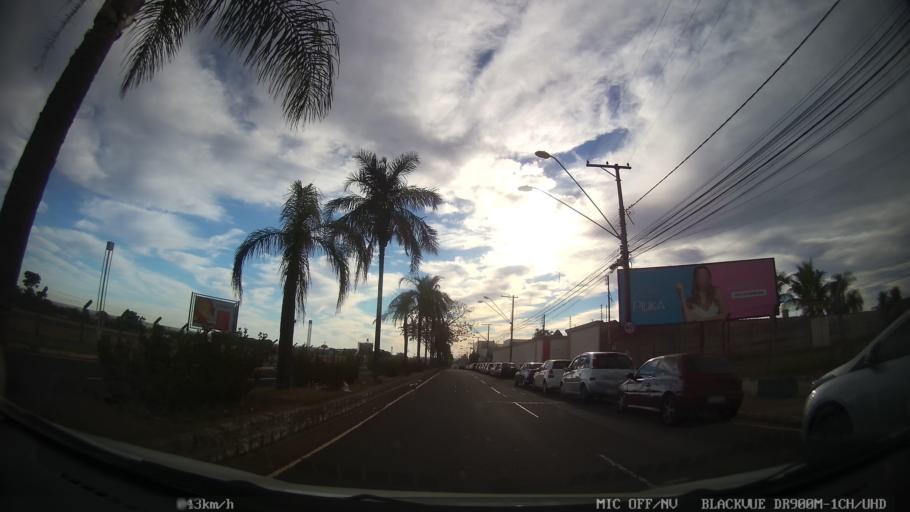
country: BR
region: Sao Paulo
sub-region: Catanduva
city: Catanduva
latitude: -21.1498
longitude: -48.9886
